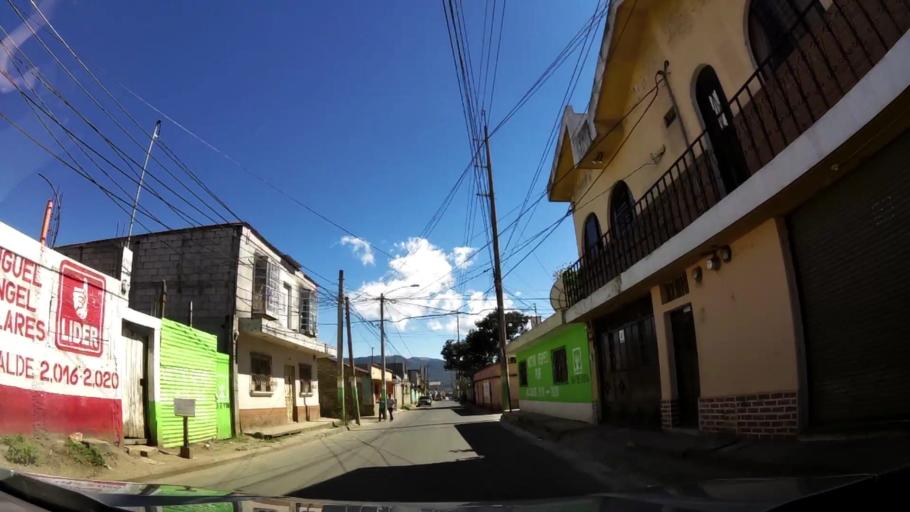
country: GT
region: Guatemala
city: San Jose Pinula
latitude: 14.5482
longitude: -90.4107
